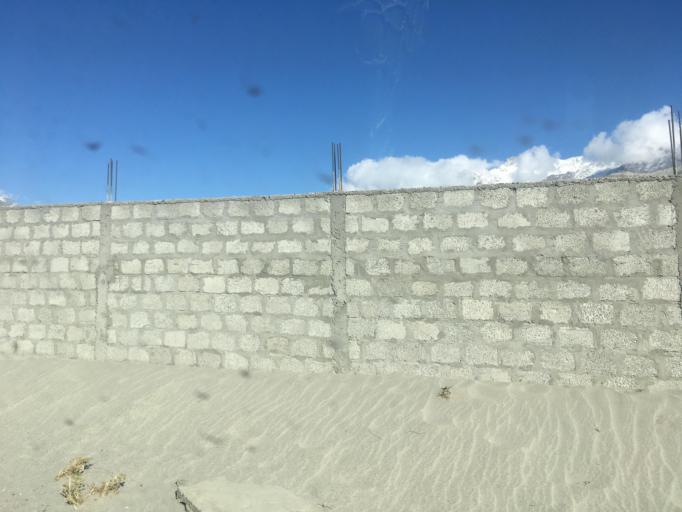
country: PK
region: Gilgit-Baltistan
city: Skardu
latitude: 35.3578
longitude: 75.5451
